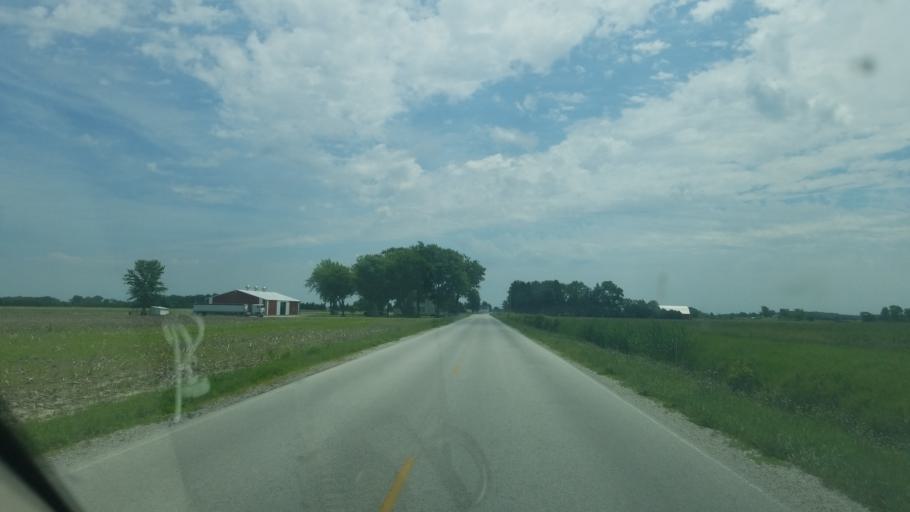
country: US
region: Ohio
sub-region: Wood County
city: Bowling Green
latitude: 41.2968
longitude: -83.6052
